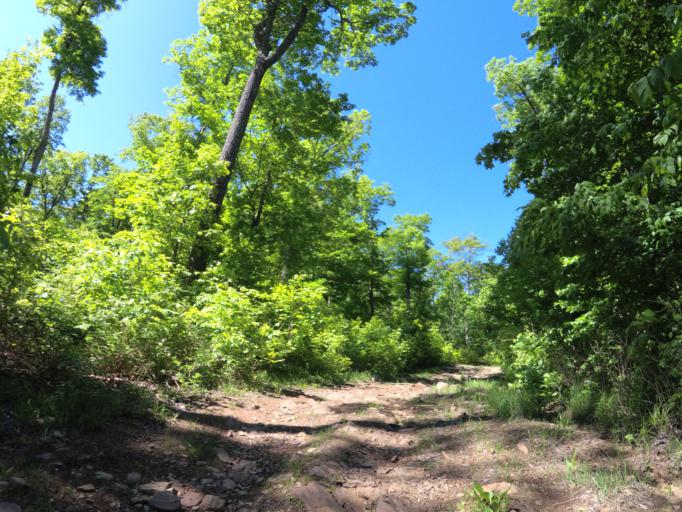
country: CA
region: Ontario
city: Renfrew
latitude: 45.0655
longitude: -77.0750
